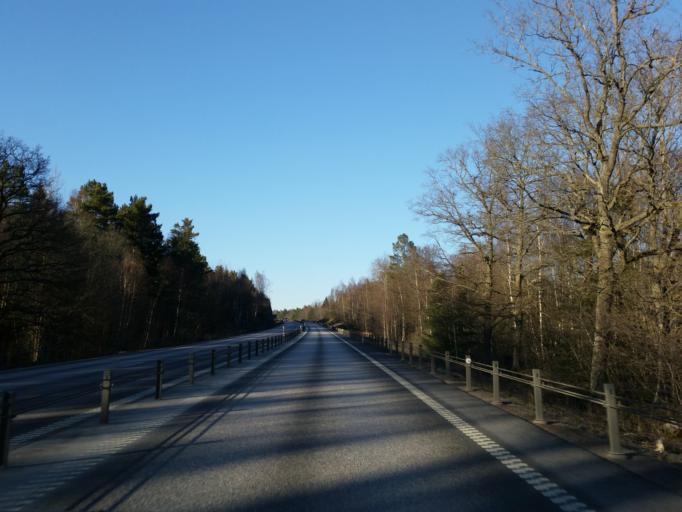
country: SE
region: Kalmar
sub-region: Oskarshamns Kommun
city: Oskarshamn
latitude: 57.2855
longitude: 16.4542
